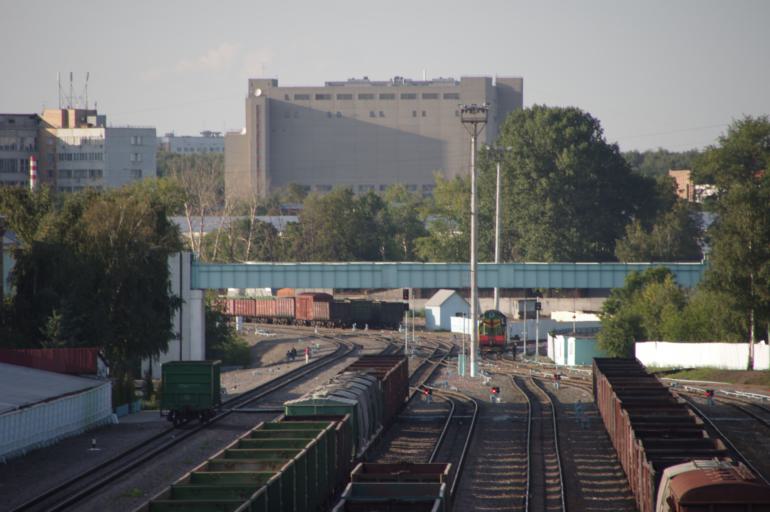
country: RU
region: Moskovskaya
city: Bogorodskoye
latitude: 55.8015
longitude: 37.7464
